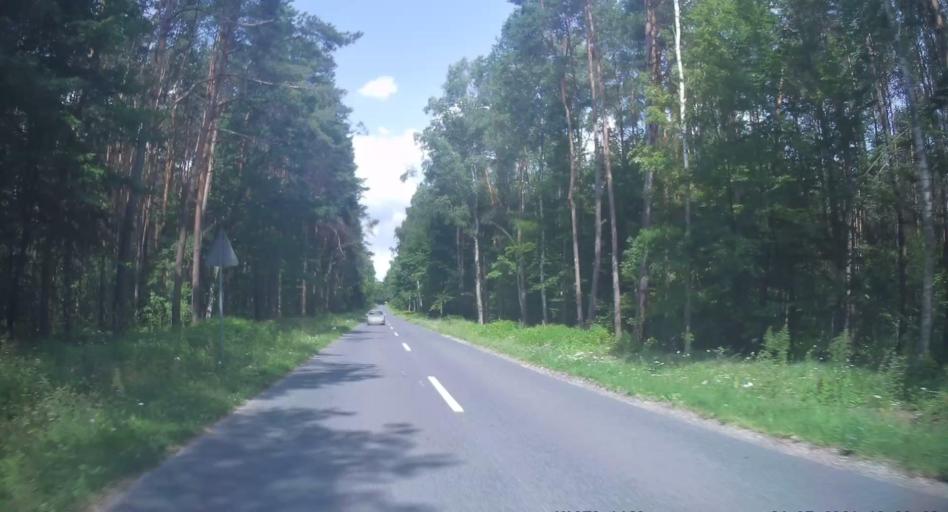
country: PL
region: Lodz Voivodeship
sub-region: Powiat tomaszowski
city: Lubochnia
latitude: 51.5589
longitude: 20.1301
